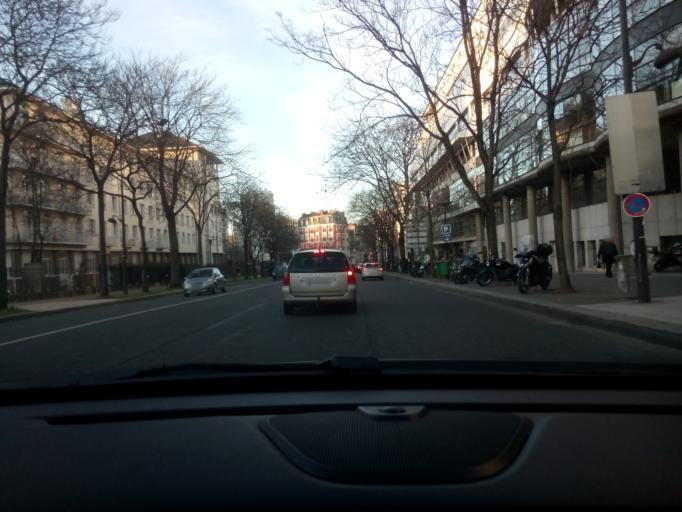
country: FR
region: Ile-de-France
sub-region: Departement du Val-de-Marne
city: Gentilly
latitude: 48.8179
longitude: 2.3441
